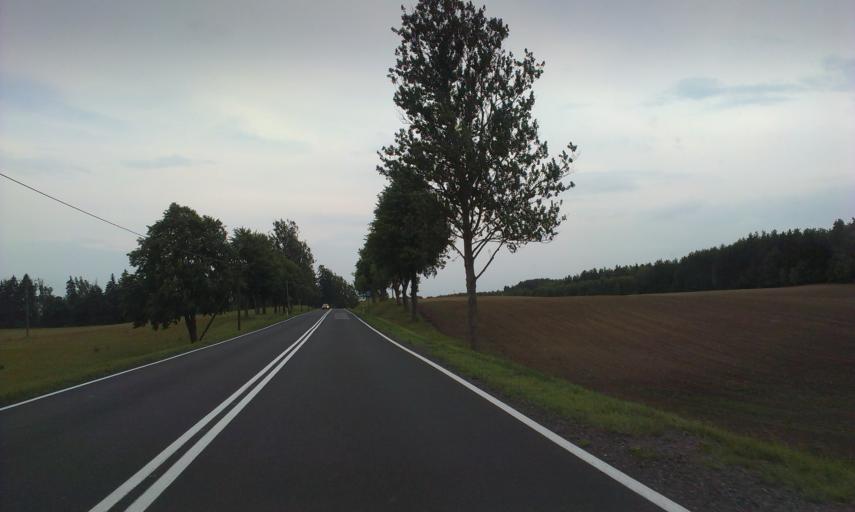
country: PL
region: West Pomeranian Voivodeship
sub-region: Powiat szczecinecki
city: Szczecinek
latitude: 53.8154
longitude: 16.6437
